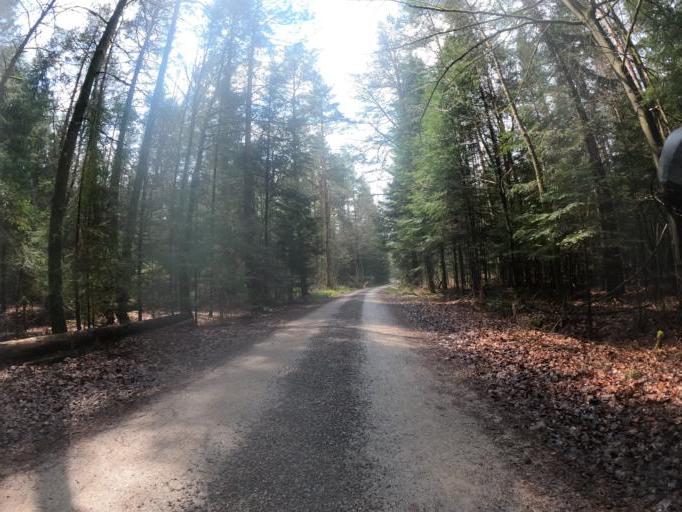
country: DE
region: Baden-Wuerttemberg
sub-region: Karlsruhe Region
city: Oberreichenbach
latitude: 48.7108
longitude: 8.6438
